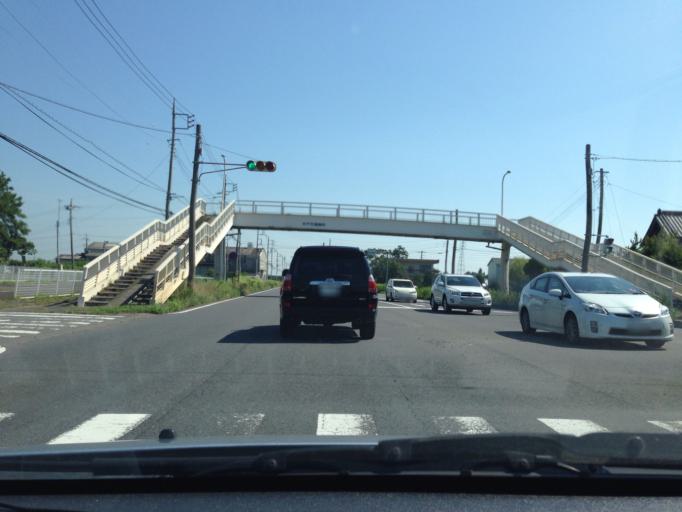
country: JP
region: Ibaraki
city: Oarai
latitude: 36.3359
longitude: 140.5568
